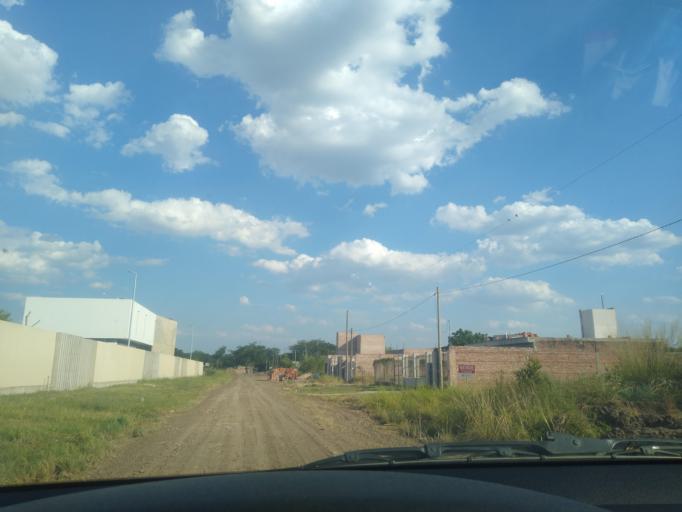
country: AR
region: Chaco
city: Resistencia
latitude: -27.4165
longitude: -58.9463
